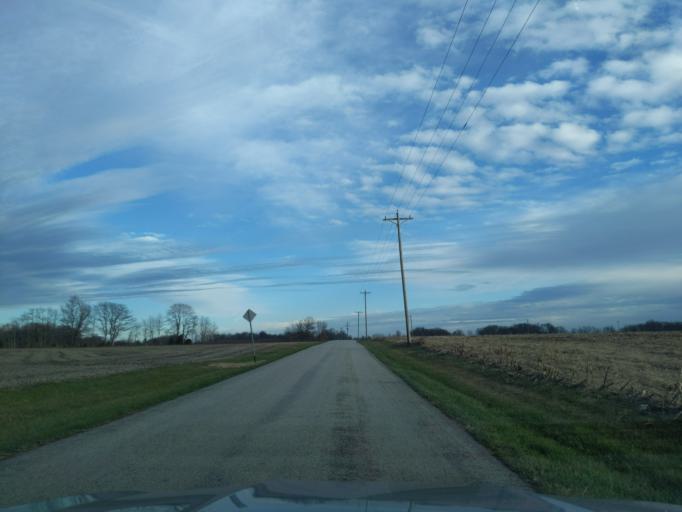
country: US
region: Indiana
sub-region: Decatur County
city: Westport
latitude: 39.2158
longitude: -85.4566
